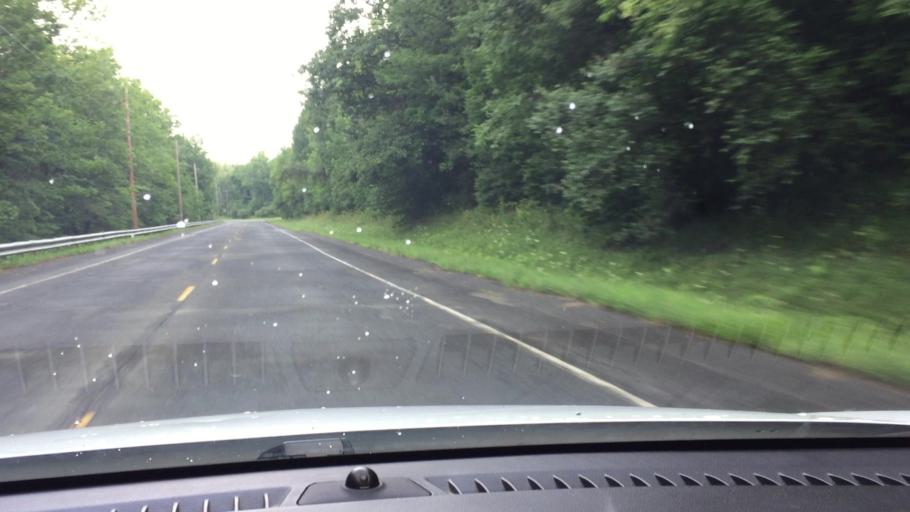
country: US
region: Massachusetts
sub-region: Berkshire County
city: Hinsdale
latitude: 42.4282
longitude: -73.0072
